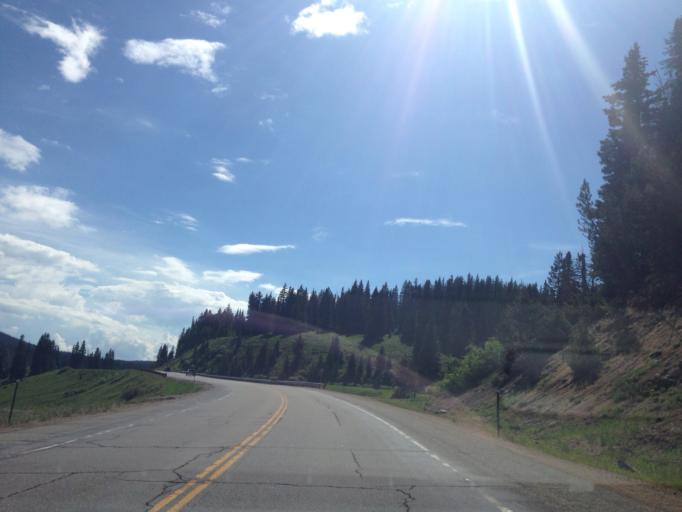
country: US
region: Colorado
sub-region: Routt County
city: Steamboat Springs
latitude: 40.3889
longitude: -106.6756
